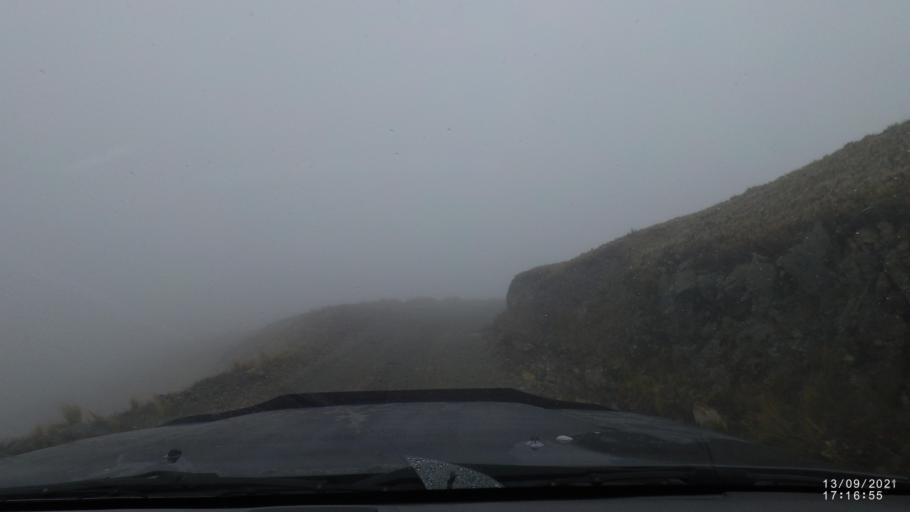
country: BO
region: Cochabamba
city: Colomi
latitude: -17.3458
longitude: -65.7596
